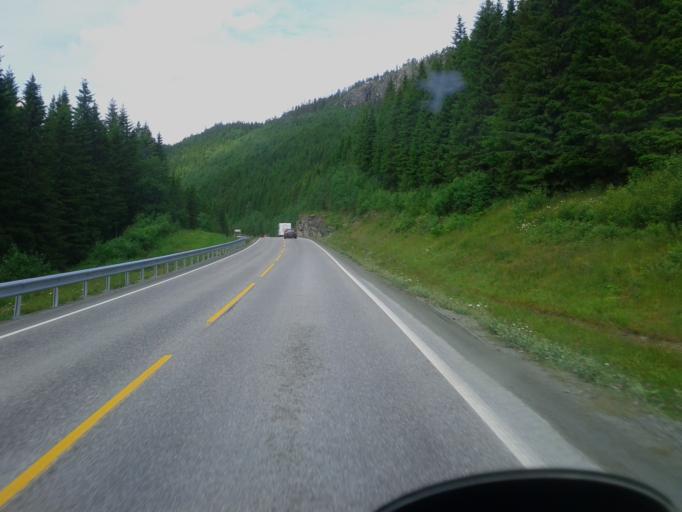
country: NO
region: Nord-Trondelag
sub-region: Grong
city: Grong
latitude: 64.5364
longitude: 12.4357
